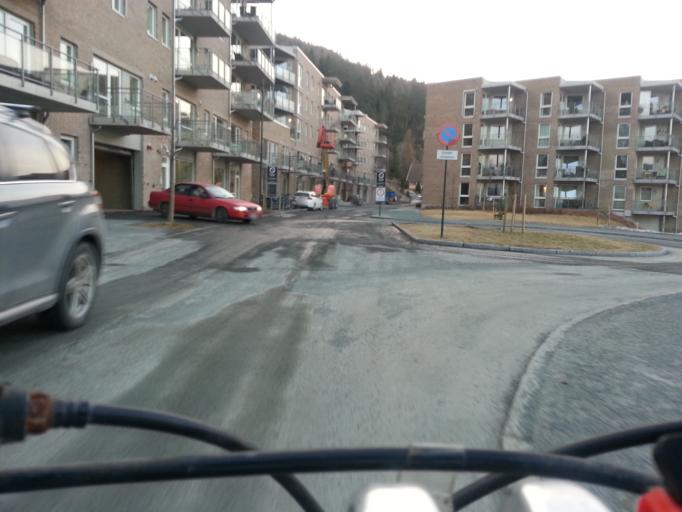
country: NO
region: Sor-Trondelag
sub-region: Trondheim
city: Trondheim
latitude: 63.4325
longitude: 10.3531
